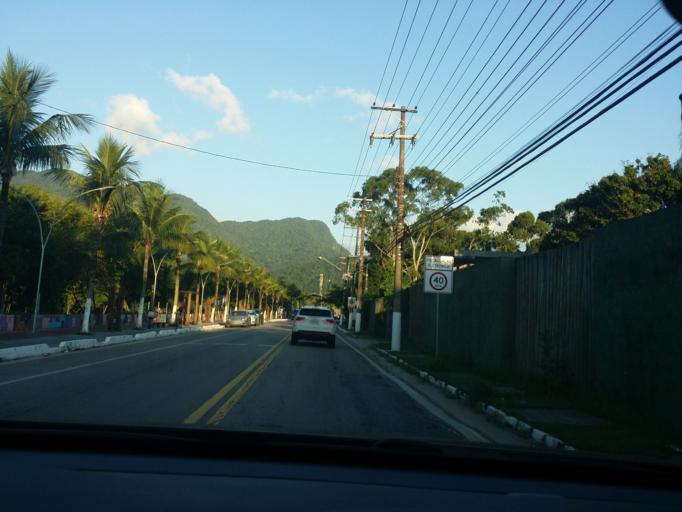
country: BR
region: Sao Paulo
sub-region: Sao Sebastiao
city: Sao Sebastiao
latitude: -23.7901
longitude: -45.5690
